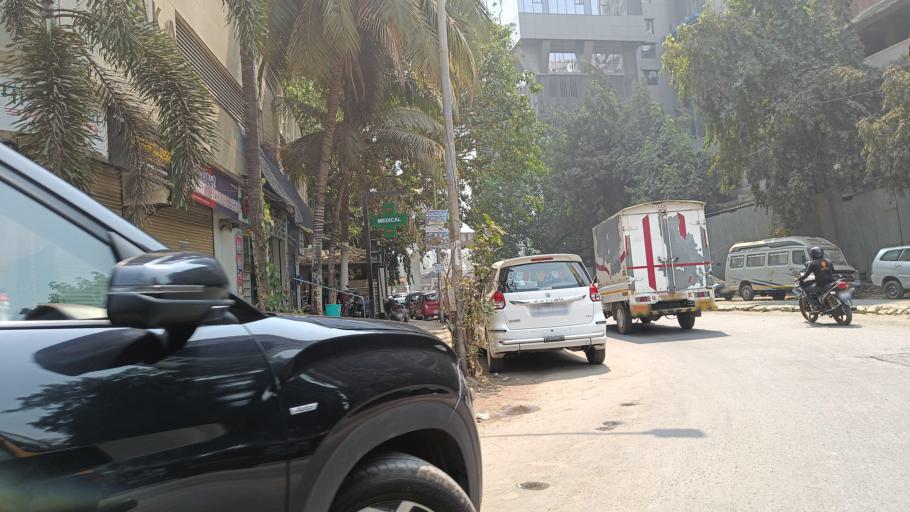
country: IN
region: Maharashtra
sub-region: Mumbai Suburban
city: Powai
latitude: 19.1525
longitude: 72.8435
